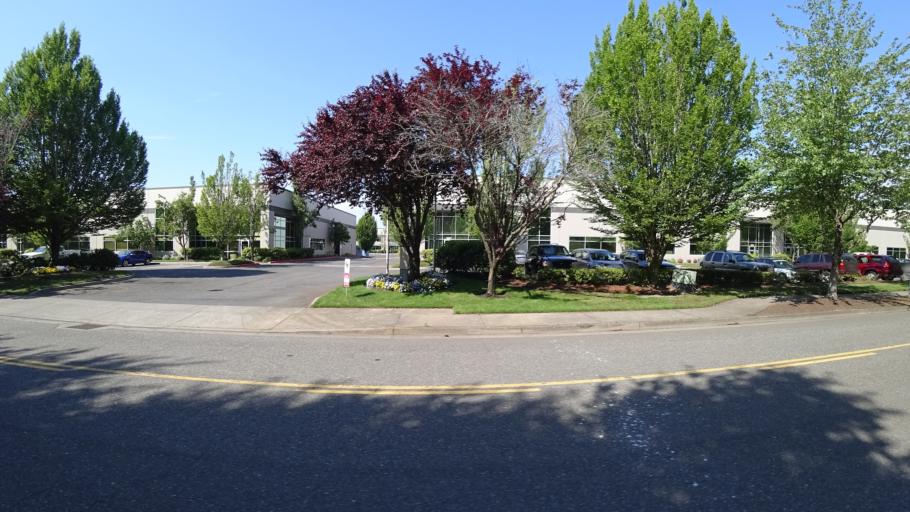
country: US
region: Oregon
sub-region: Multnomah County
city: Fairview
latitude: 45.5589
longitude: -122.4978
